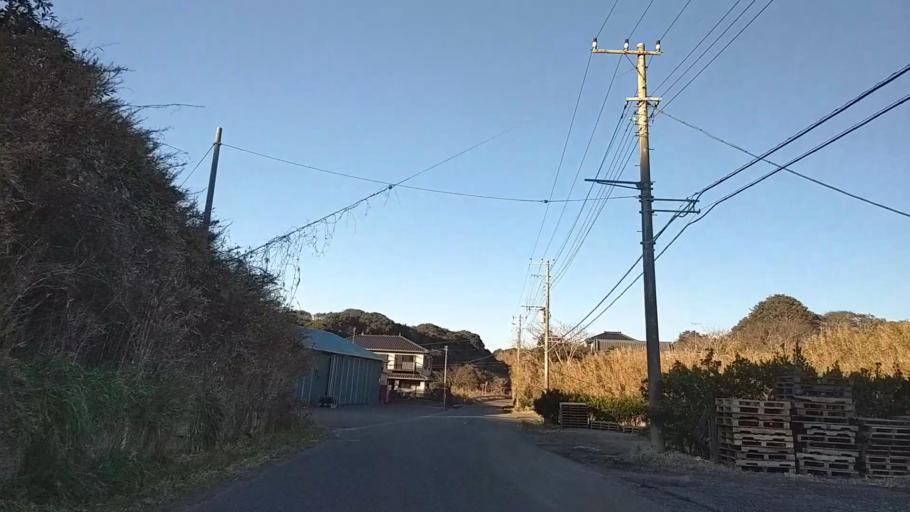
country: JP
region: Chiba
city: Asahi
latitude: 35.7096
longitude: 140.7280
